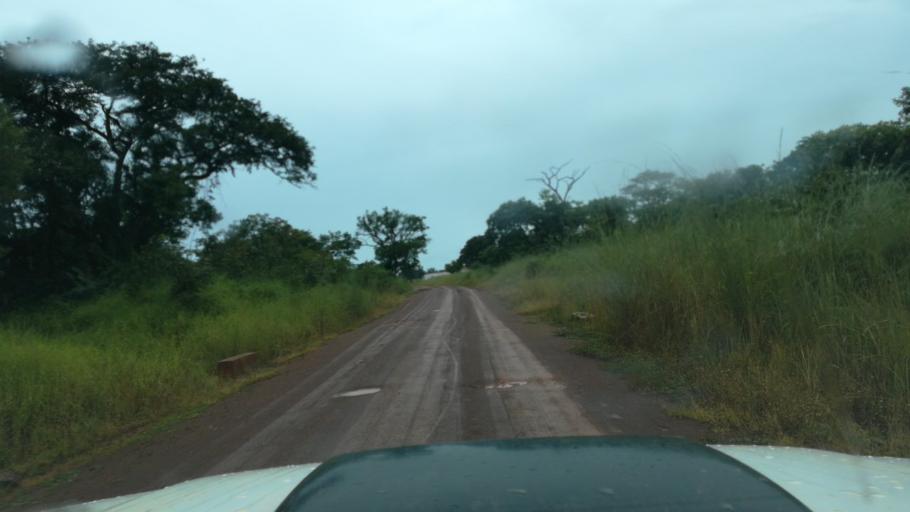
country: ZM
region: Luapula
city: Mwense
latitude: -10.2990
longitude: 28.1197
